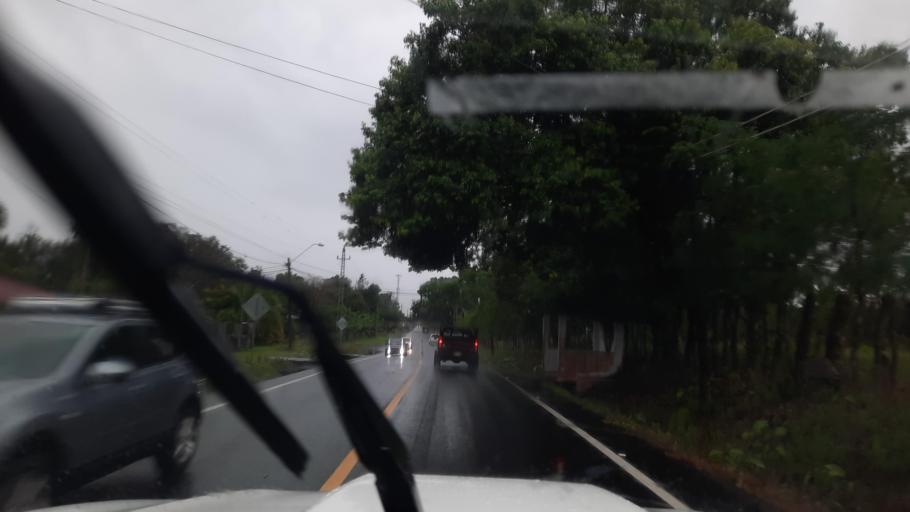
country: PA
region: Chiriqui
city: Sortova
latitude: 8.5595
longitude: -82.6278
